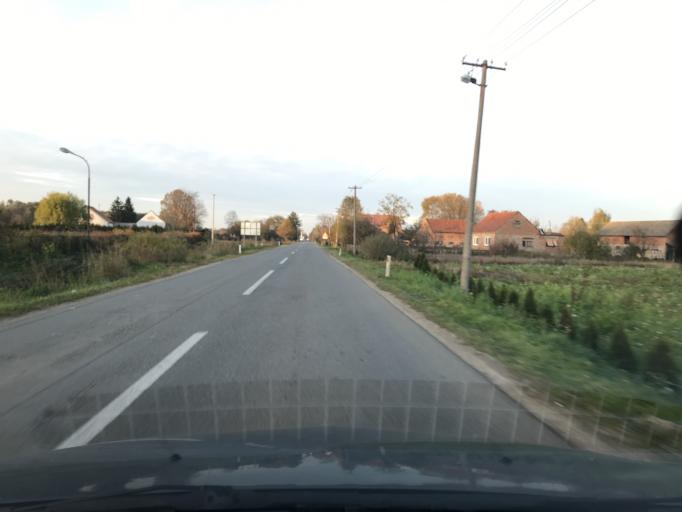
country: BA
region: Republika Srpska
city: Bosanska Dubica
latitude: 45.2093
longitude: 16.9041
